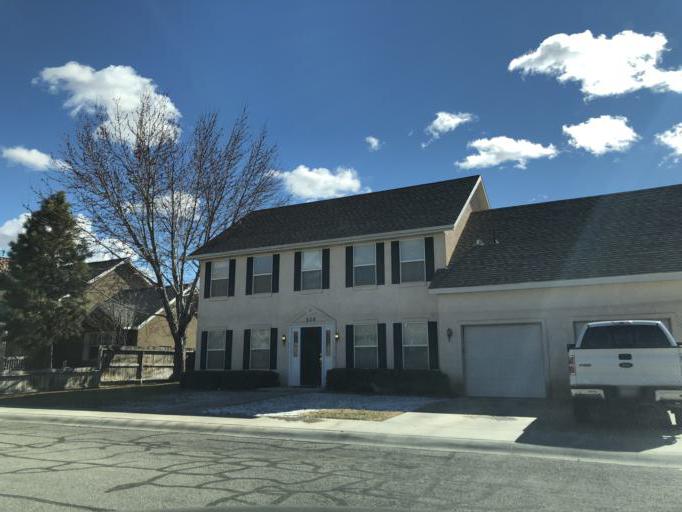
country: US
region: Utah
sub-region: Grand County
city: Moab
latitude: 38.5816
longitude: -109.5632
